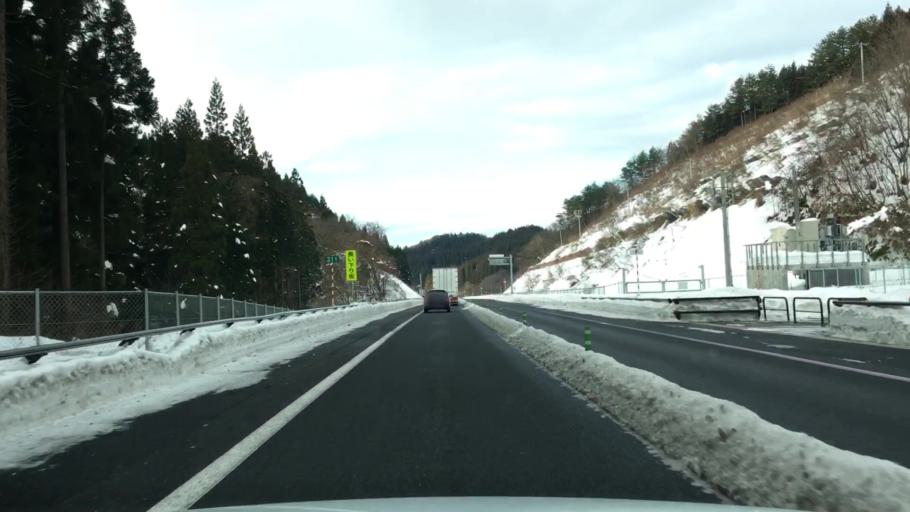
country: JP
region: Akita
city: Takanosu
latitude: 40.2255
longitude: 140.4498
